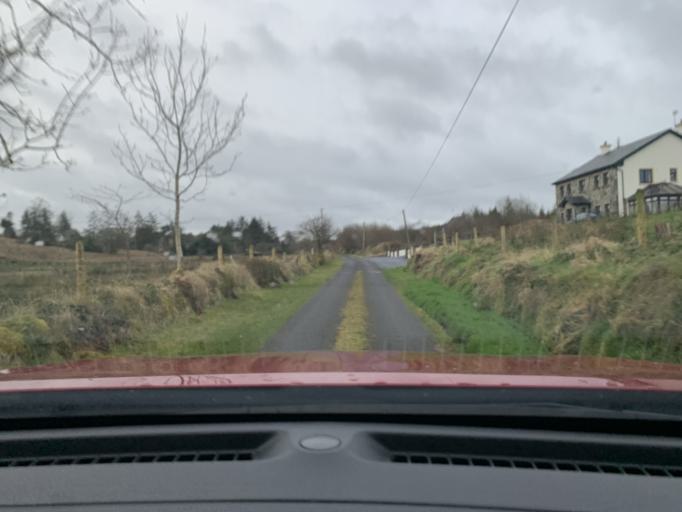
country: IE
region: Connaught
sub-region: Roscommon
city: Boyle
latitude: 54.0057
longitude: -8.3978
